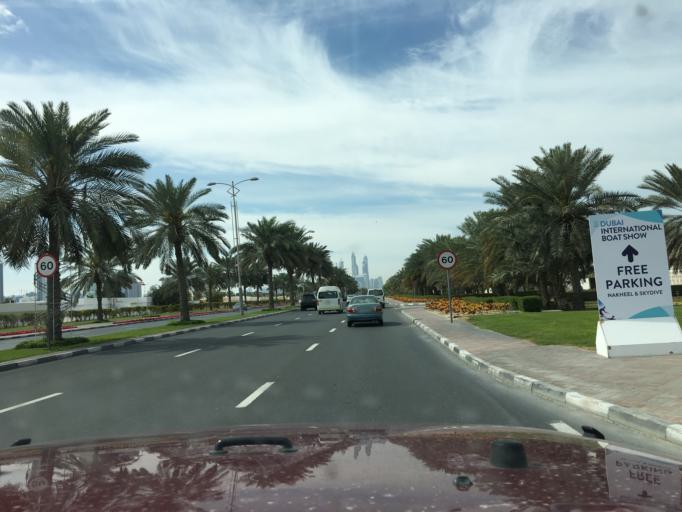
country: AE
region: Dubai
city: Dubai
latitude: 25.1270
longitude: 55.1829
